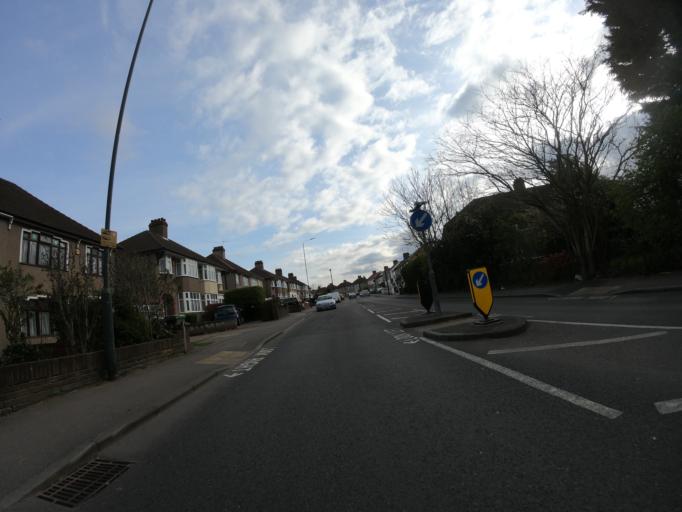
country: GB
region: England
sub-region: Greater London
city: Bexleyheath
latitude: 51.4767
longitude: 0.1451
